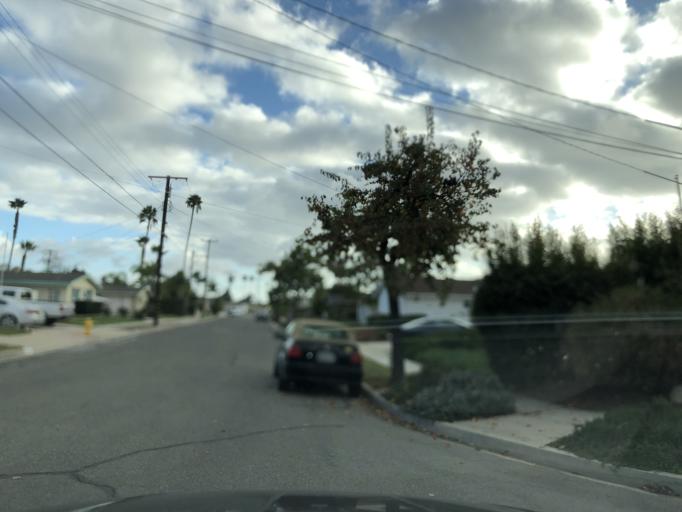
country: US
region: California
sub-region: San Diego County
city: La Jolla
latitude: 32.8145
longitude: -117.1860
